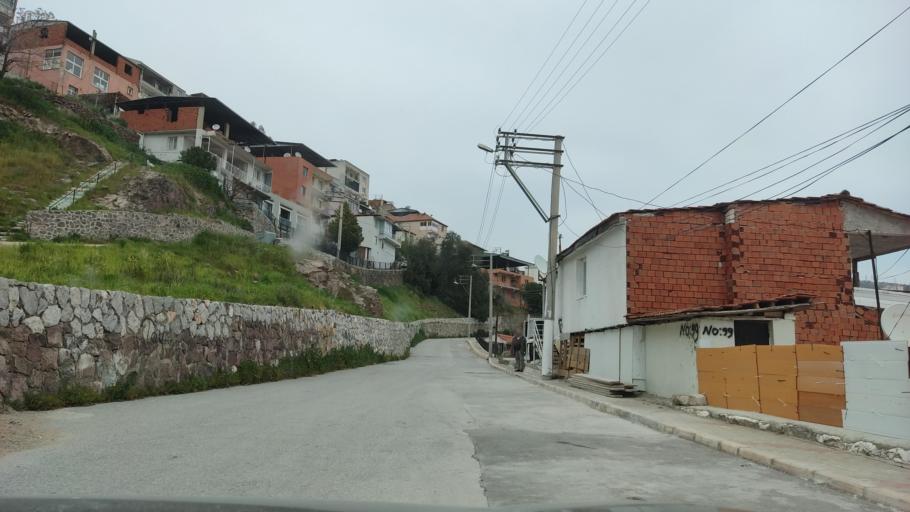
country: TR
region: Izmir
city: Karsiyaka
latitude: 38.4968
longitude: 27.0759
